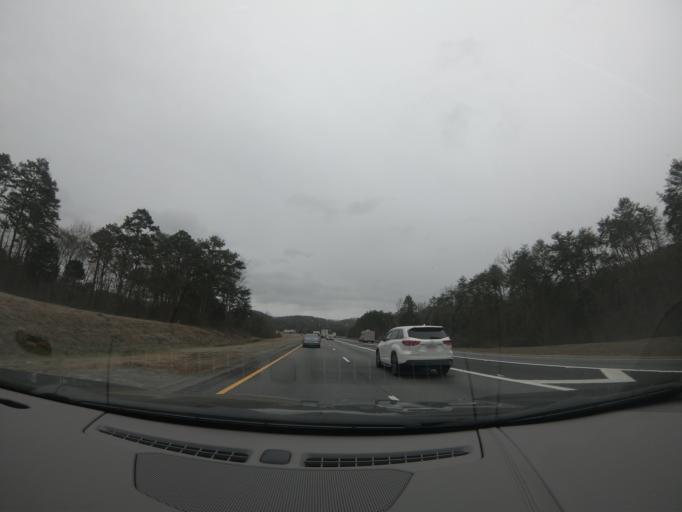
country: US
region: Georgia
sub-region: Walker County
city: Lookout Mountain
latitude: 34.9748
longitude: -85.4552
